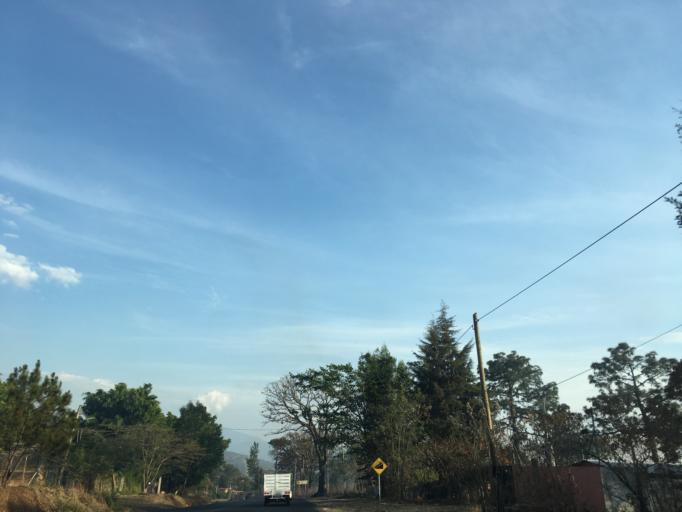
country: MX
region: Michoacan
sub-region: Los Reyes
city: La Higuerita (Colonia San Rafael)
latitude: 19.6746
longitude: -102.4937
